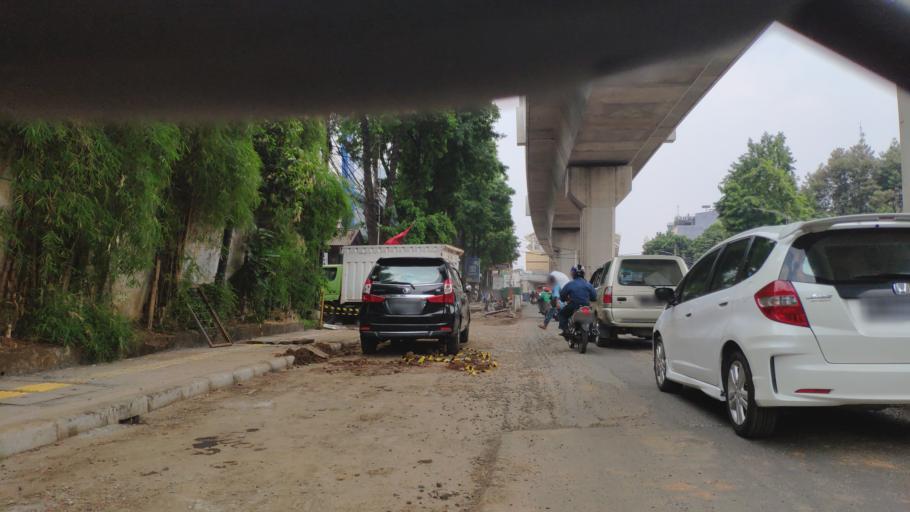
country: ID
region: Jakarta Raya
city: Jakarta
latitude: -6.2691
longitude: 106.7973
